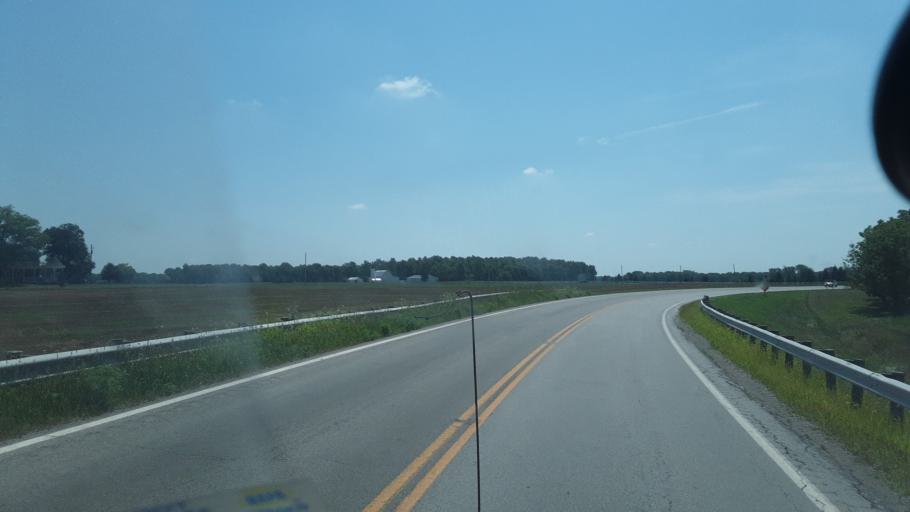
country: US
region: Ohio
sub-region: Hancock County
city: Arlington
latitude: 40.9231
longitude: -83.5559
